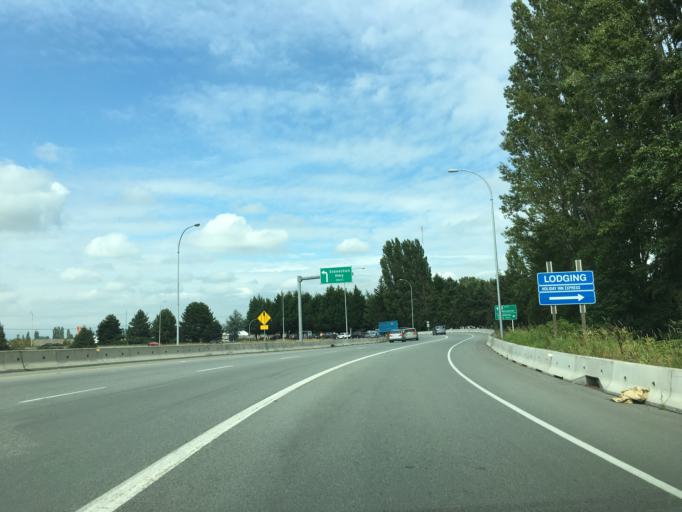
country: CA
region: British Columbia
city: Ladner
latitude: 49.1316
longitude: -123.0858
